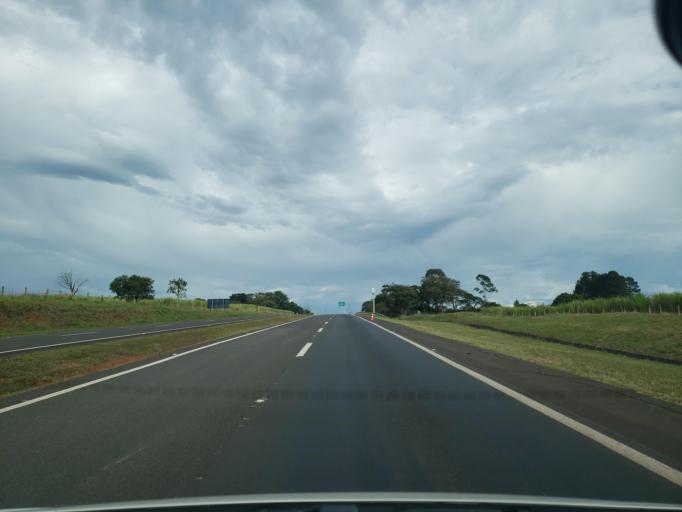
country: BR
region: Sao Paulo
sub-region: Dois Corregos
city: Dois Corregos
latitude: -22.2594
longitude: -48.3700
